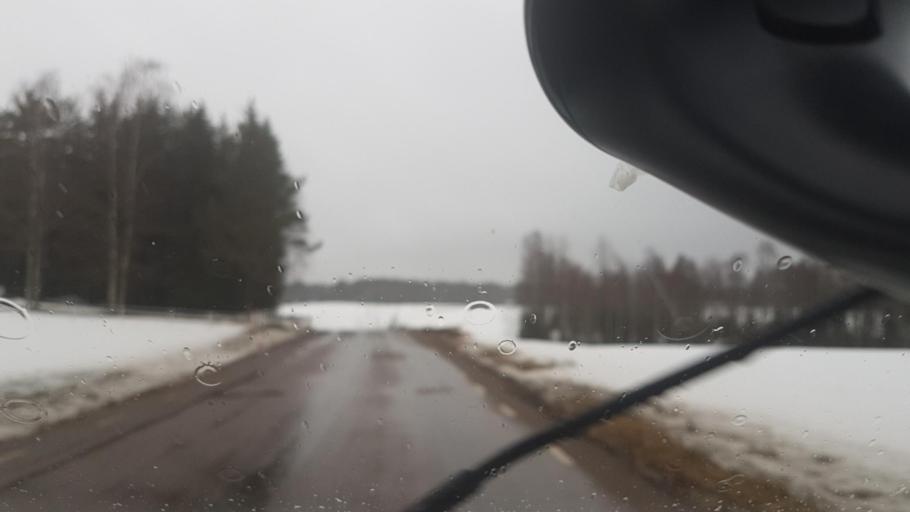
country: SE
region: Vaermland
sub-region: Eda Kommun
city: Charlottenberg
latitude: 59.8698
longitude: 12.3497
